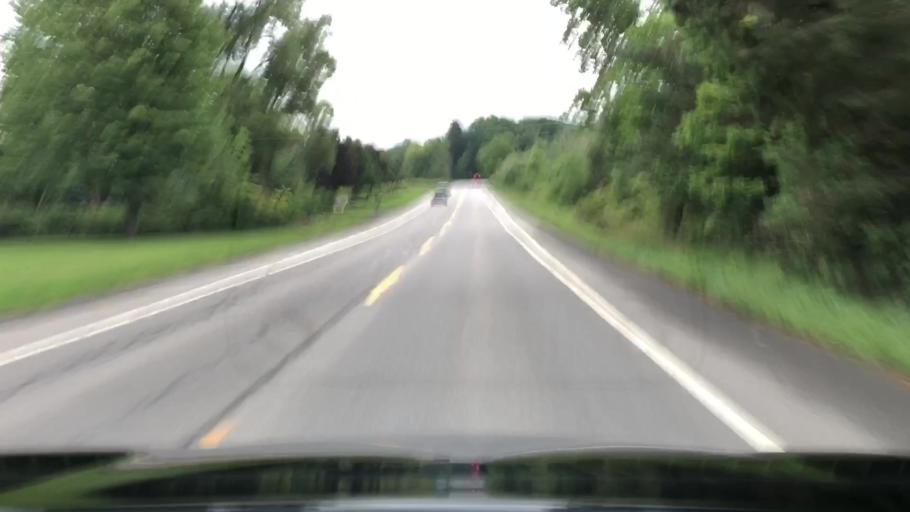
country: US
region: New York
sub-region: Erie County
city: Orchard Park
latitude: 42.7559
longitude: -78.6969
